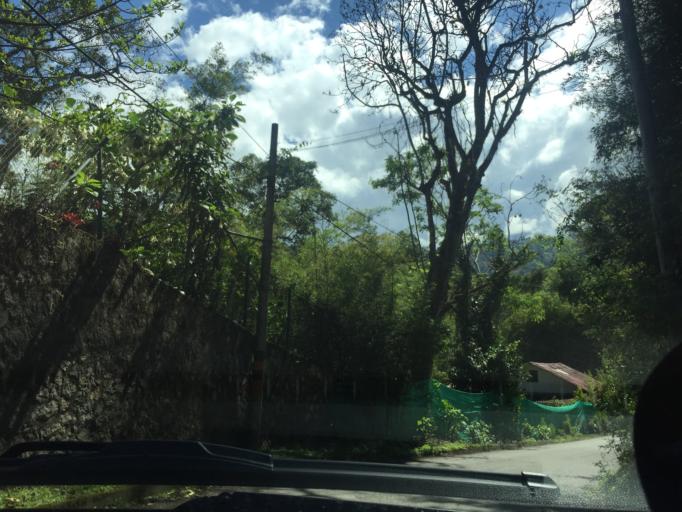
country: CO
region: Cundinamarca
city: San Francisco
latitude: 4.9849
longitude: -74.2891
